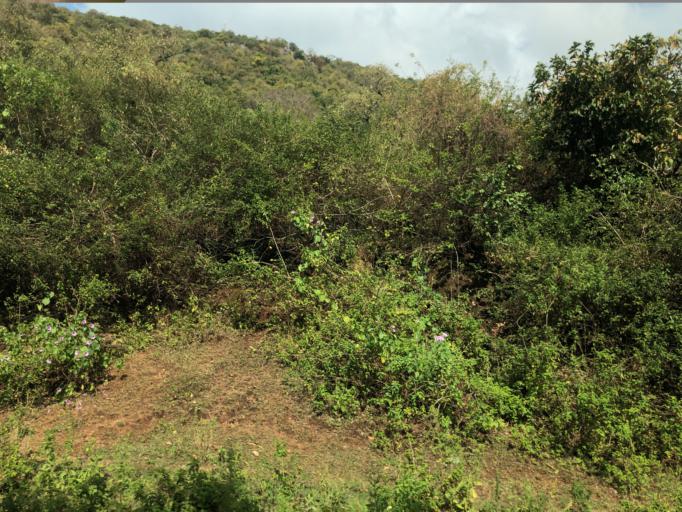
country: ET
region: Southern Nations, Nationalities, and People's Region
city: Bako
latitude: 5.7504
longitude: 36.5899
